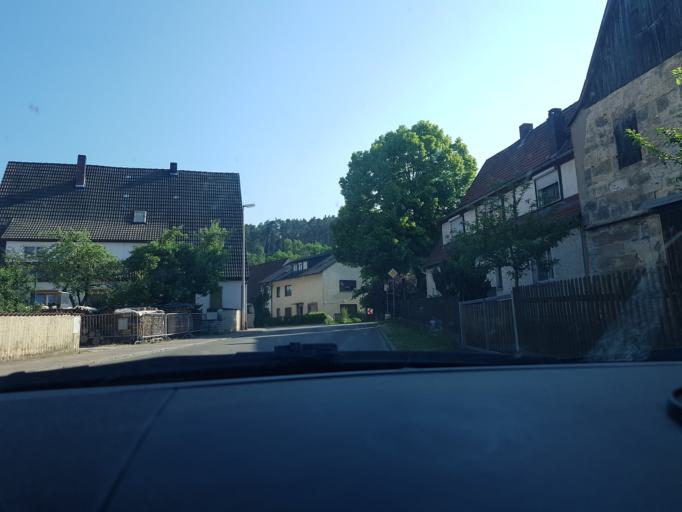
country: DE
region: Bavaria
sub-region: Regierungsbezirk Mittelfranken
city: Georgensgmund
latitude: 49.2036
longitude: 11.0510
